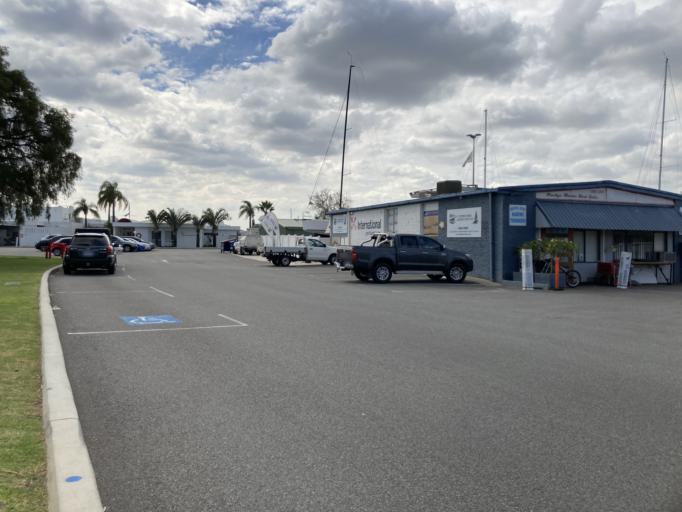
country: AU
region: Western Australia
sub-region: Melville
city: Applecross
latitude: -32.0030
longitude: 115.8454
